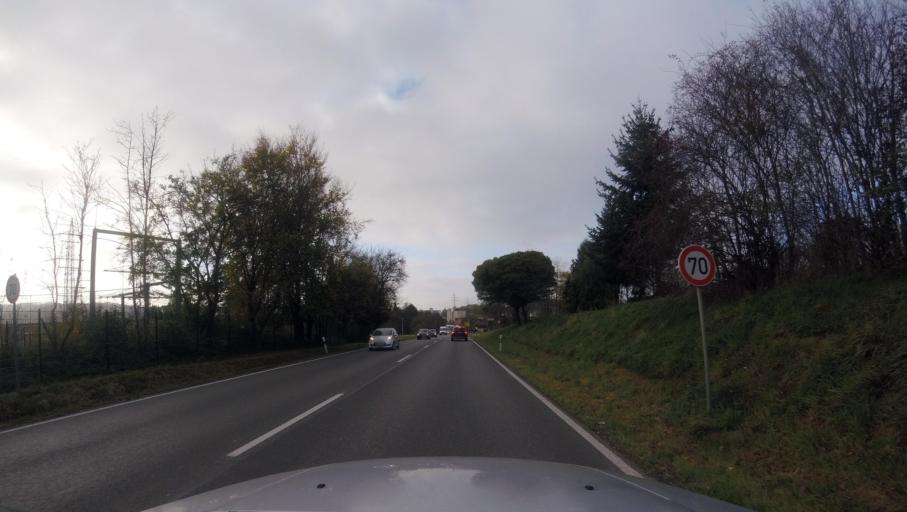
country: DE
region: Baden-Wuerttemberg
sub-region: Regierungsbezirk Stuttgart
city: Backnang
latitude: 48.9257
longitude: 9.4334
